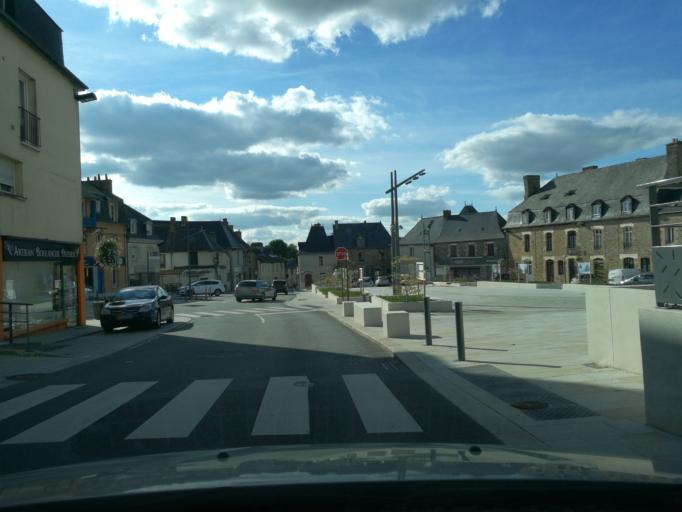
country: FR
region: Brittany
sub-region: Departement d'Ille-et-Vilaine
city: Montauban-de-Bretagne
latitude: 48.2007
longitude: -2.0463
